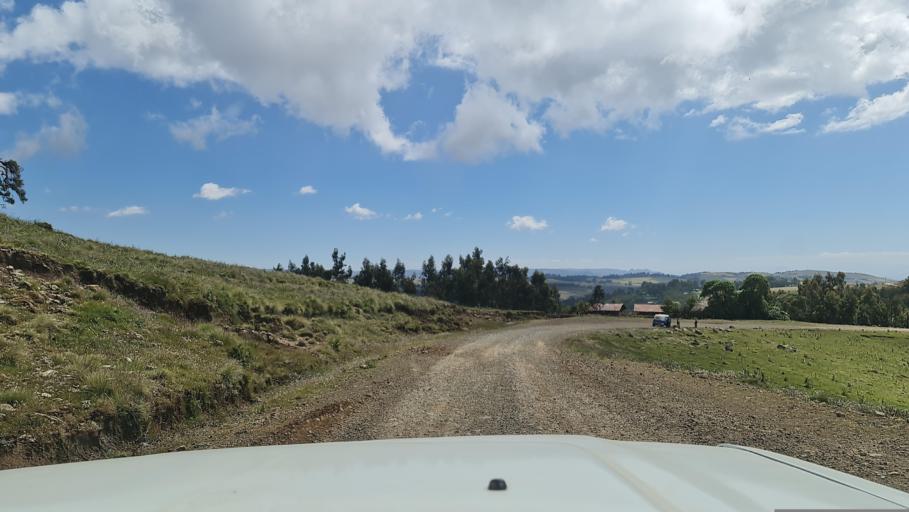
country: ET
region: Amhara
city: Debark'
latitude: 13.2092
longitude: 37.9730
